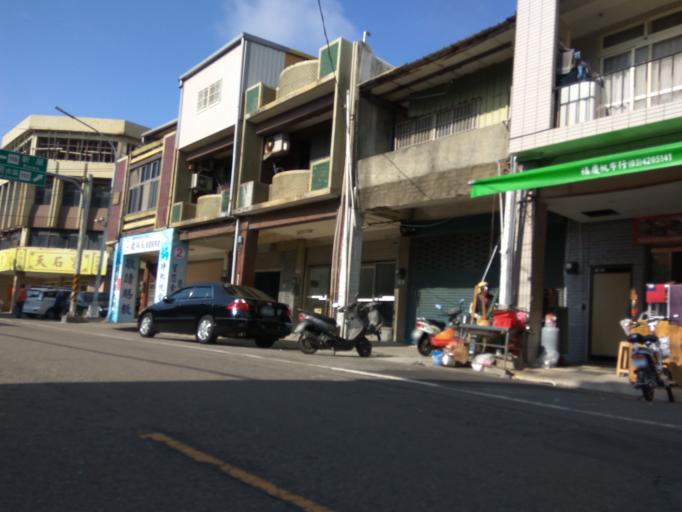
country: TW
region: Taiwan
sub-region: Hsinchu
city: Zhubei
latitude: 25.0357
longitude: 121.0836
